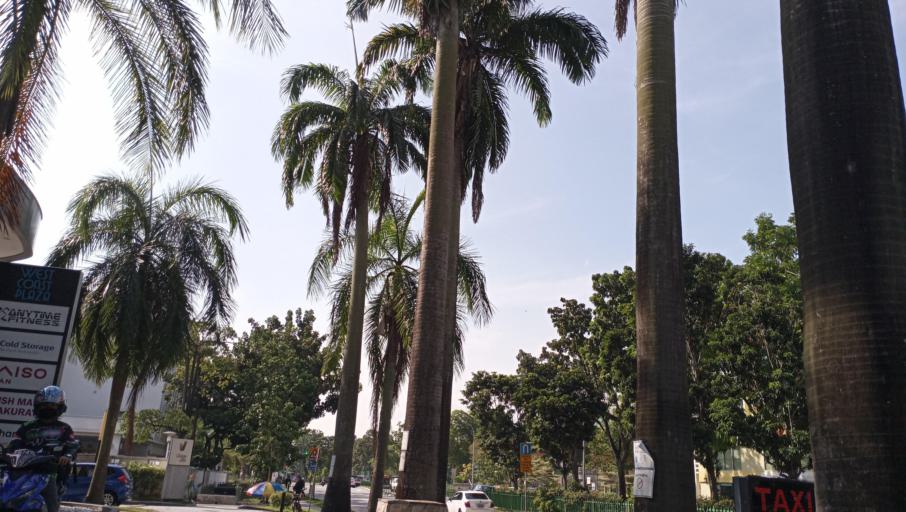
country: SG
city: Singapore
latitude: 1.3033
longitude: 103.7653
